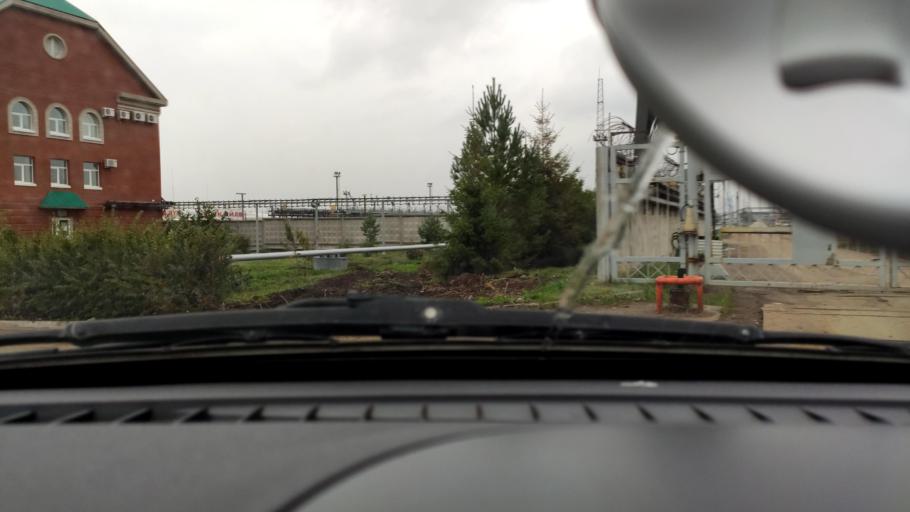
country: RU
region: Perm
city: Gamovo
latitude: 57.9073
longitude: 56.1504
